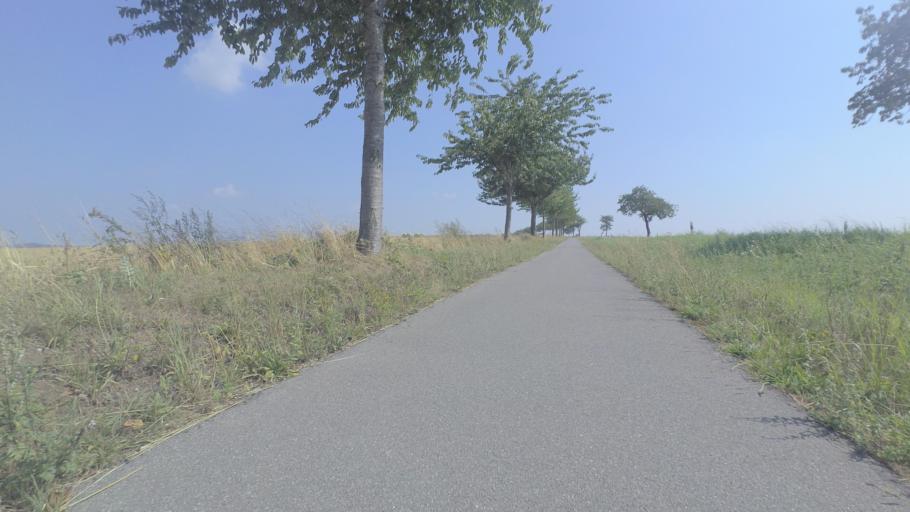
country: DE
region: Mecklenburg-Vorpommern
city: Gielow
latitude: 53.7220
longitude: 12.7069
